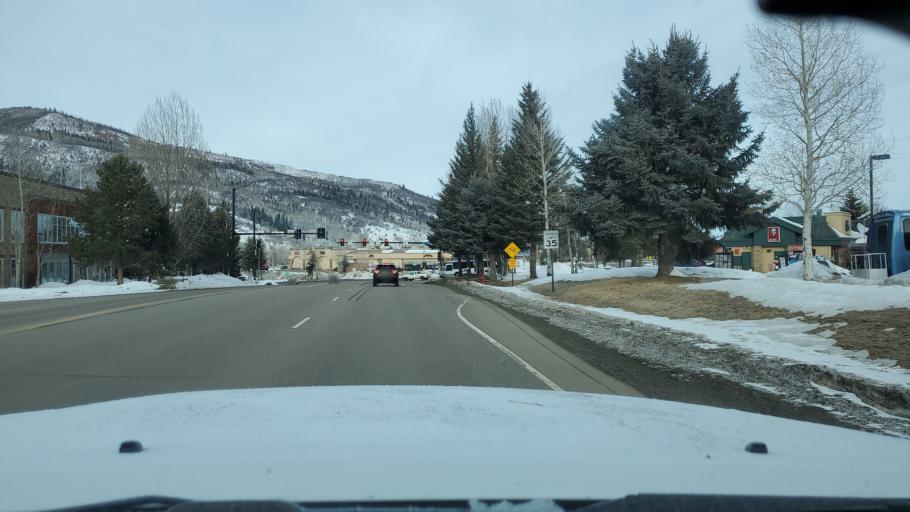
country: US
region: Colorado
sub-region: Routt County
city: Steamboat Springs
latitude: 40.4593
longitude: -106.8191
